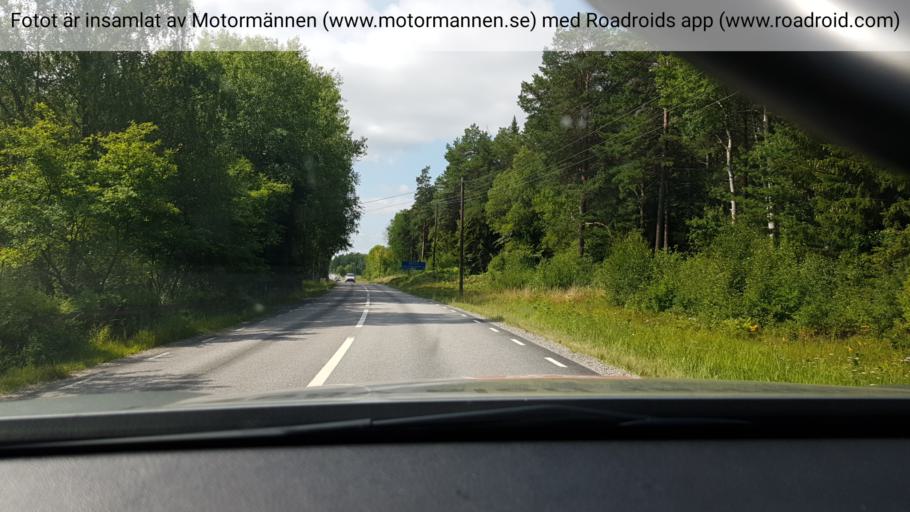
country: SE
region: Stockholm
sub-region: Osterakers Kommun
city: Akersberga
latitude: 59.5540
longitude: 18.2174
